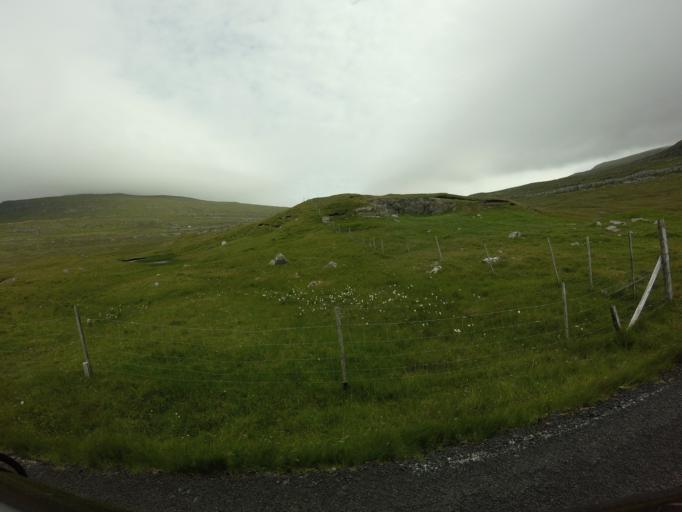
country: FO
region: Sandoy
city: Sandur
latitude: 61.8182
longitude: -6.7482
